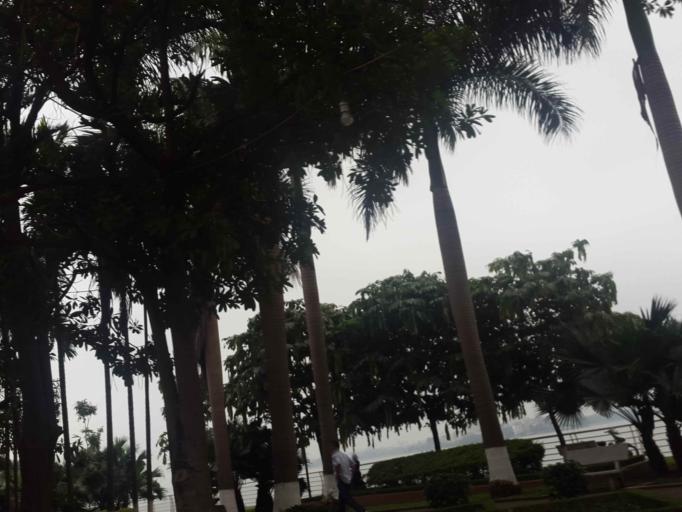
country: VN
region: Ha Noi
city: Cau Giay
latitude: 21.0462
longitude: 105.8148
